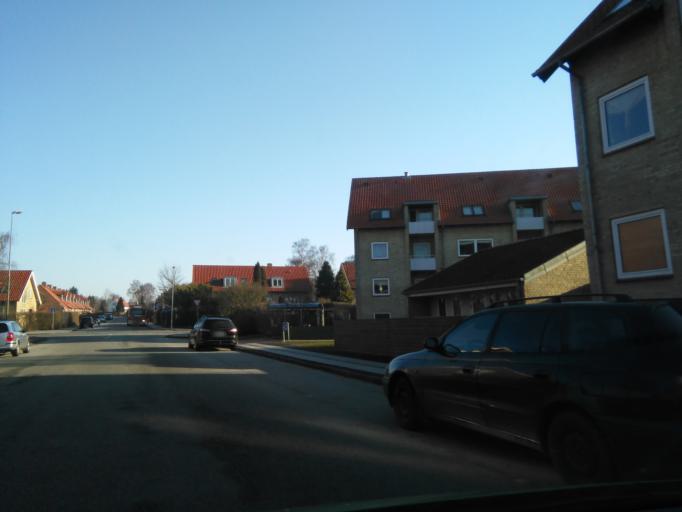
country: DK
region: Central Jutland
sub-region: Arhus Kommune
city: Arhus
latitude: 56.1210
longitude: 10.1924
